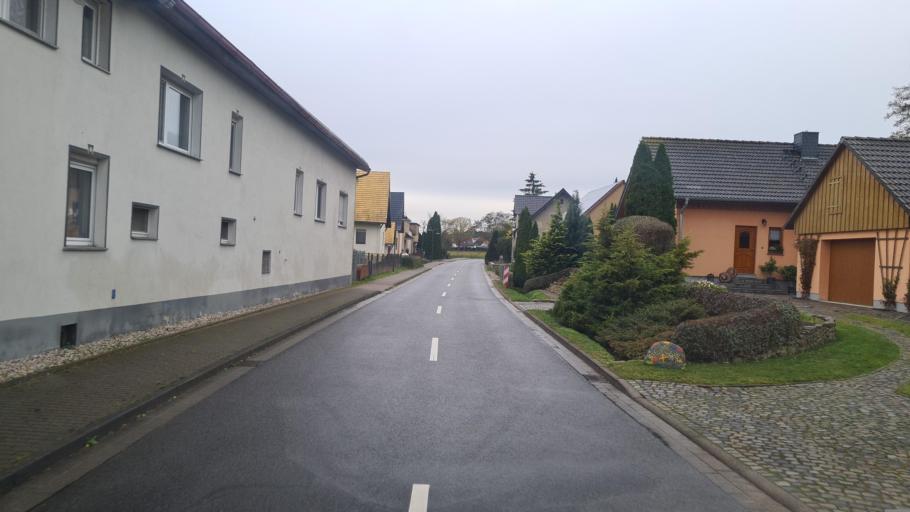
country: DE
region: Saxony-Anhalt
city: Abtsdorf
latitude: 51.9290
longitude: 12.6734
